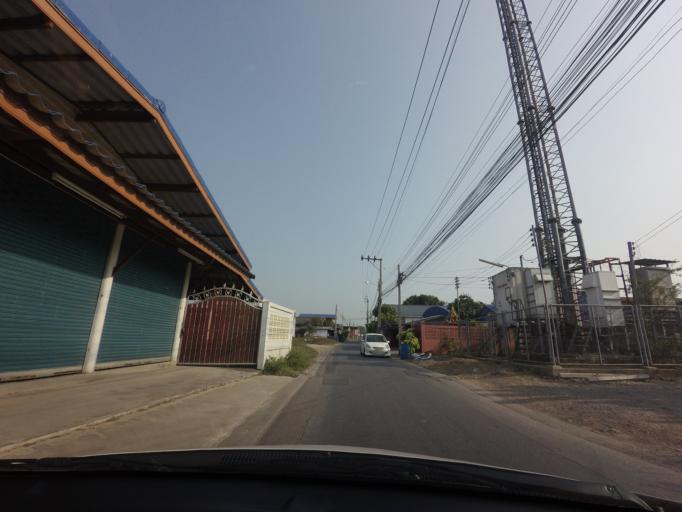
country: TH
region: Nonthaburi
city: Bang Yai
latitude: 13.8066
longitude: 100.3728
